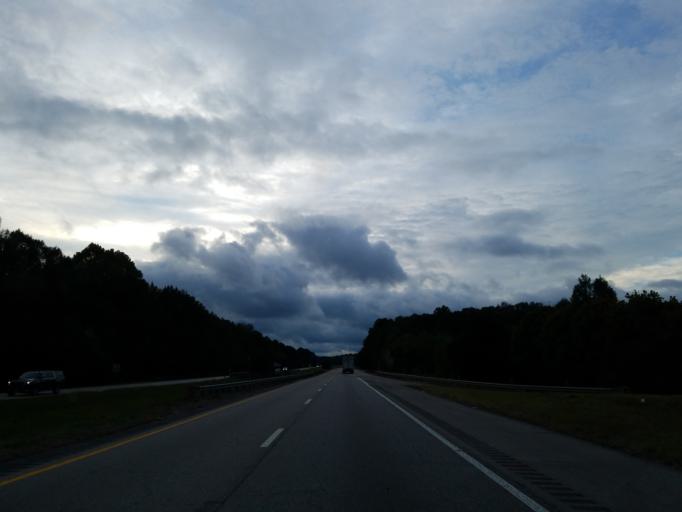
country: US
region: Mississippi
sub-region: Lauderdale County
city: Marion
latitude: 32.4136
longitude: -88.5073
